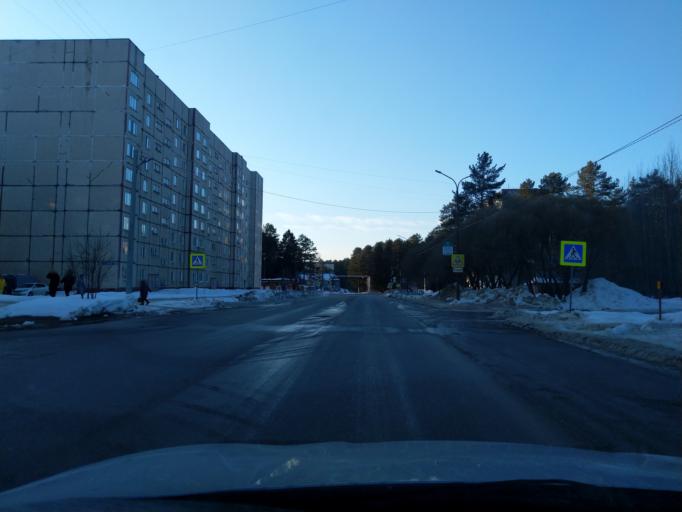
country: RU
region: Perm
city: Dobryanka
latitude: 58.4696
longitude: 56.3973
